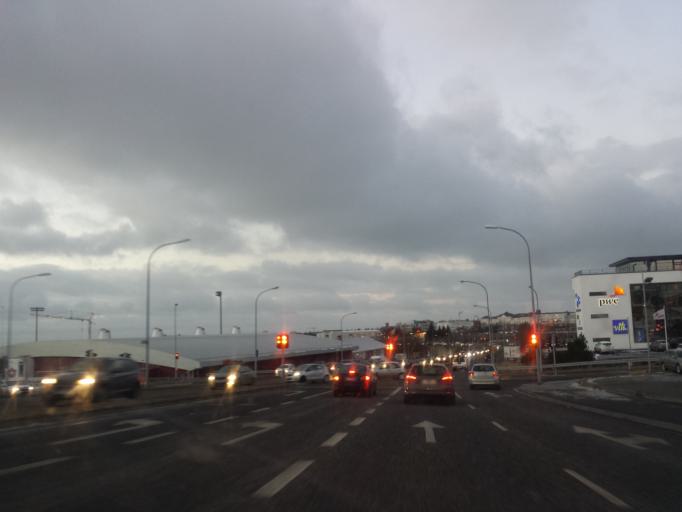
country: IS
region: Capital Region
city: Kopavogur
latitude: 64.1323
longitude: -21.9197
